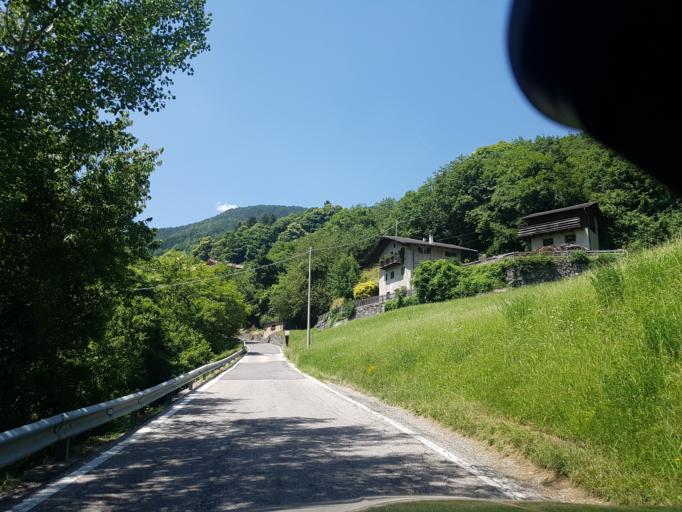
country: IT
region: Trentino-Alto Adige
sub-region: Bolzano
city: Villandro - Villanders
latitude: 46.6222
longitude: 11.5271
